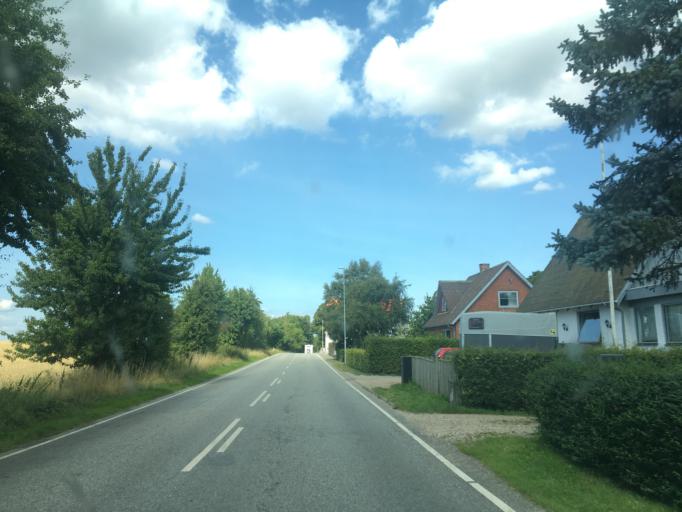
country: DK
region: South Denmark
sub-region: Middelfart Kommune
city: Ejby
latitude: 55.4214
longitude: 9.9222
